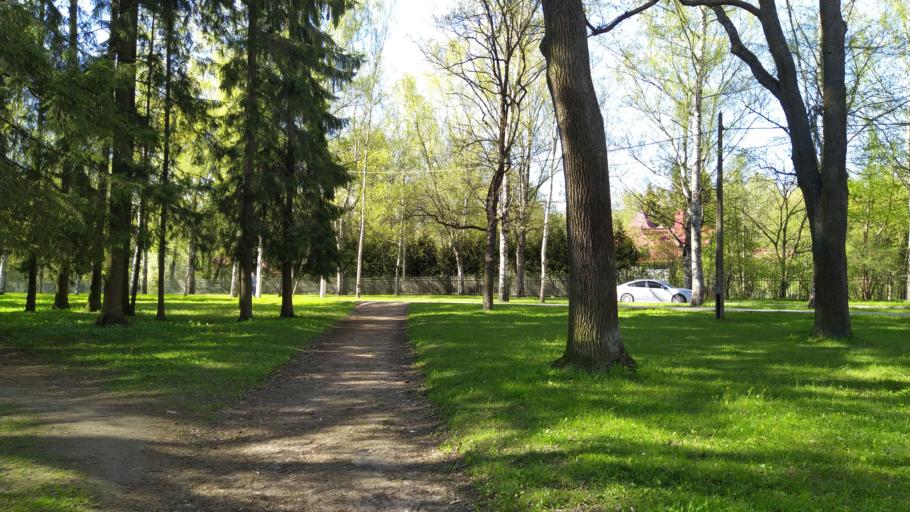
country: RU
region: St.-Petersburg
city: Pavlovsk
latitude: 59.6881
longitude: 30.4392
